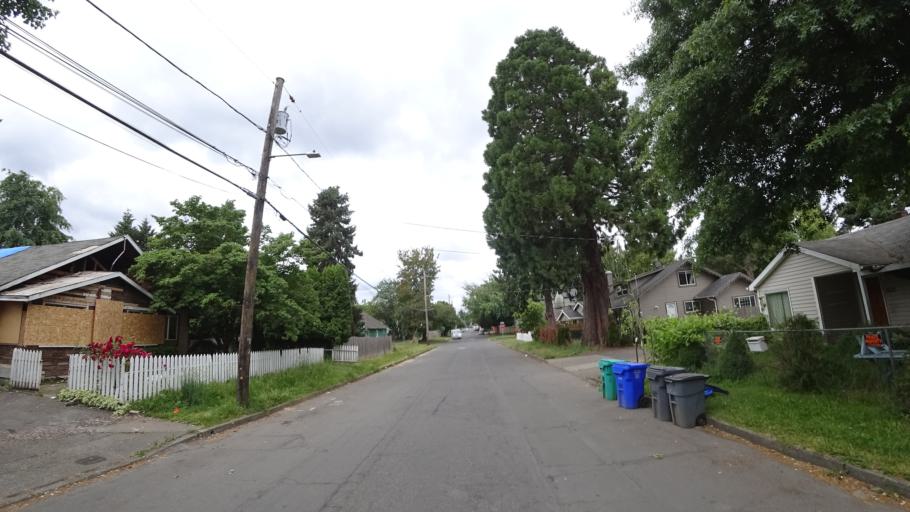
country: US
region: Oregon
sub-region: Multnomah County
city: Lents
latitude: 45.5005
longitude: -122.5742
